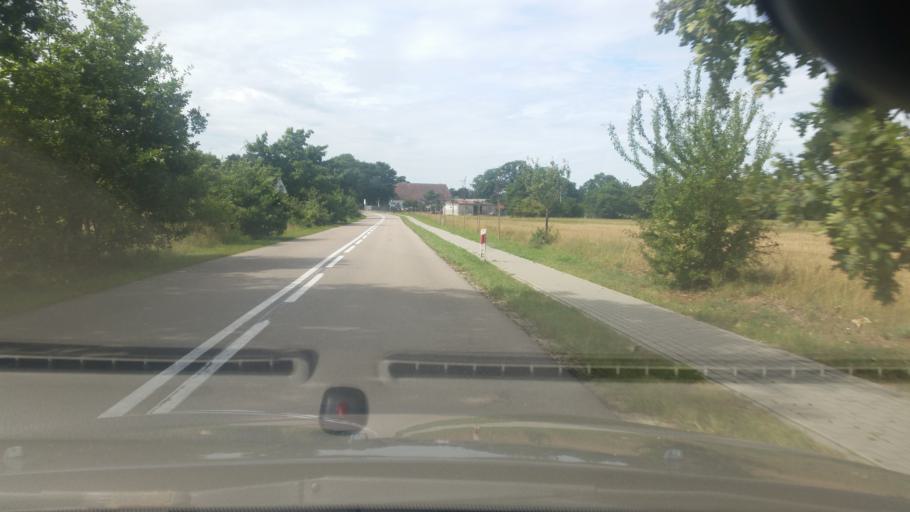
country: PL
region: Pomeranian Voivodeship
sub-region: Powiat leborski
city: Leba
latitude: 54.7524
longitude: 17.6742
